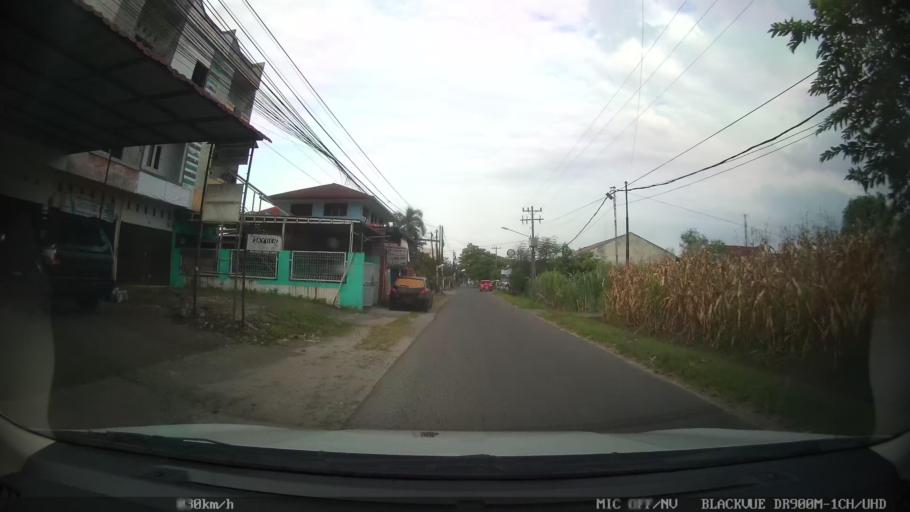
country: ID
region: North Sumatra
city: Sunggal
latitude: 3.5549
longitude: 98.6273
